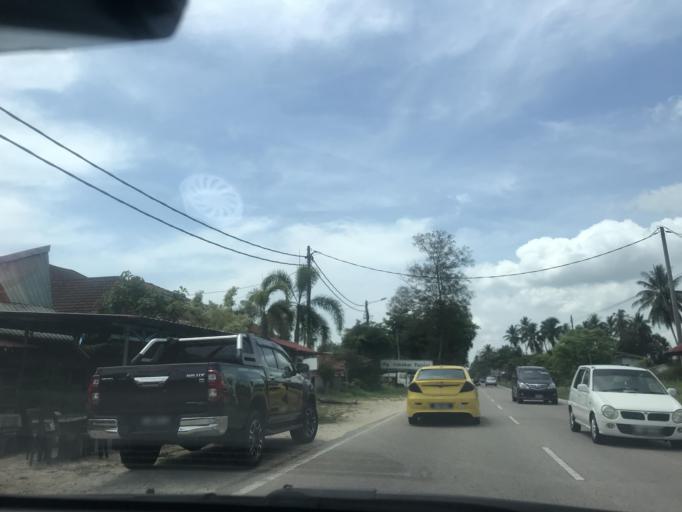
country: MY
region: Kelantan
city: Tumpat
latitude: 6.2095
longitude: 102.1377
